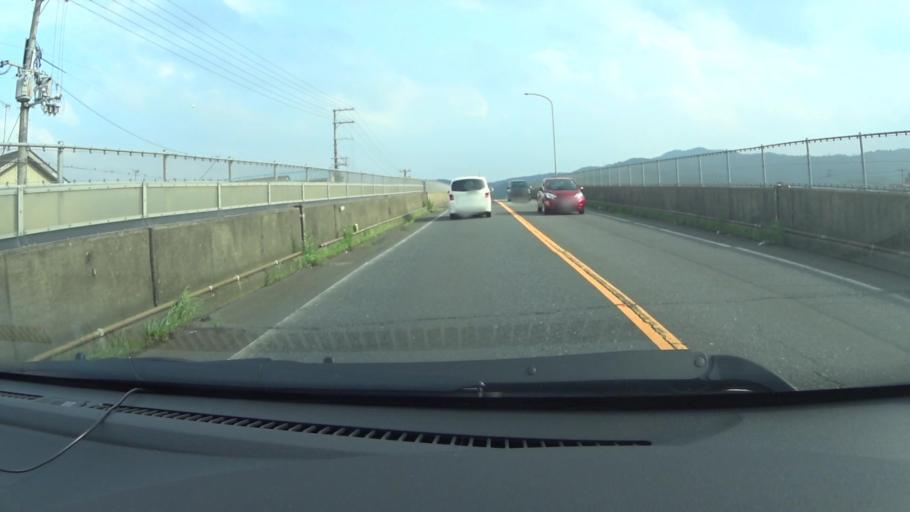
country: JP
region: Kyoto
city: Maizuru
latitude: 35.4350
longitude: 135.3282
